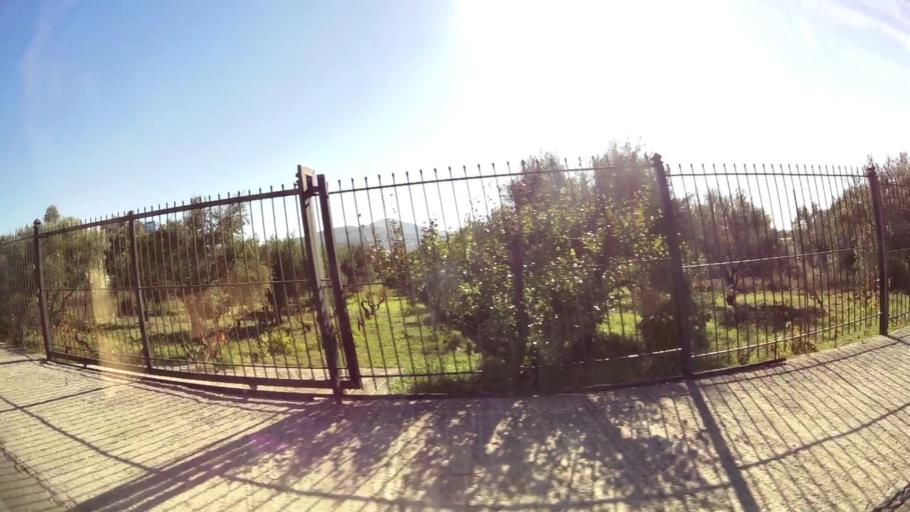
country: GR
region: Attica
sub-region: Nomarchia Anatolikis Attikis
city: Varybobi
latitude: 38.1062
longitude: 23.7887
